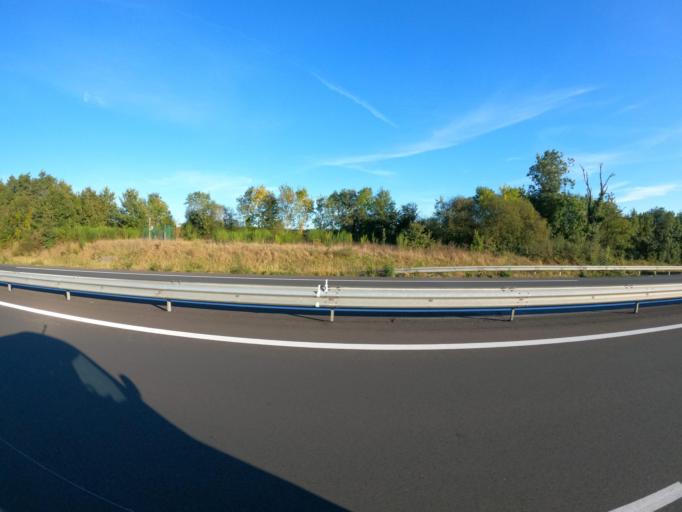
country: FR
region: Pays de la Loire
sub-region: Departement de la Vendee
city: Beaurepaire
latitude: 46.8836
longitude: -1.1050
